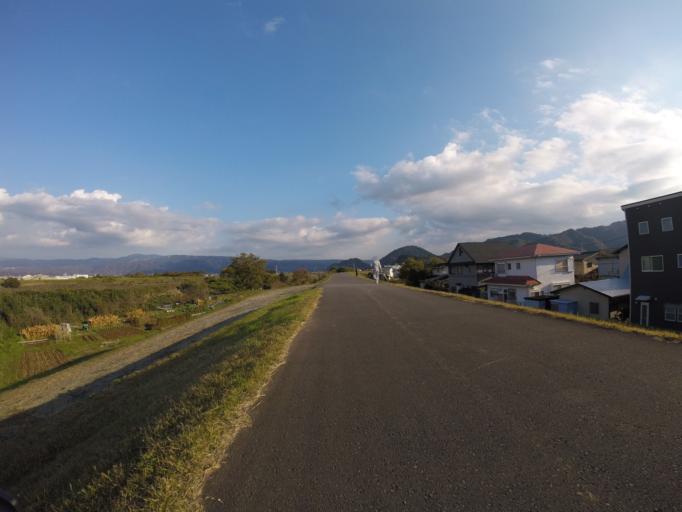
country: JP
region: Shizuoka
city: Mishima
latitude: 35.0804
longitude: 138.9096
